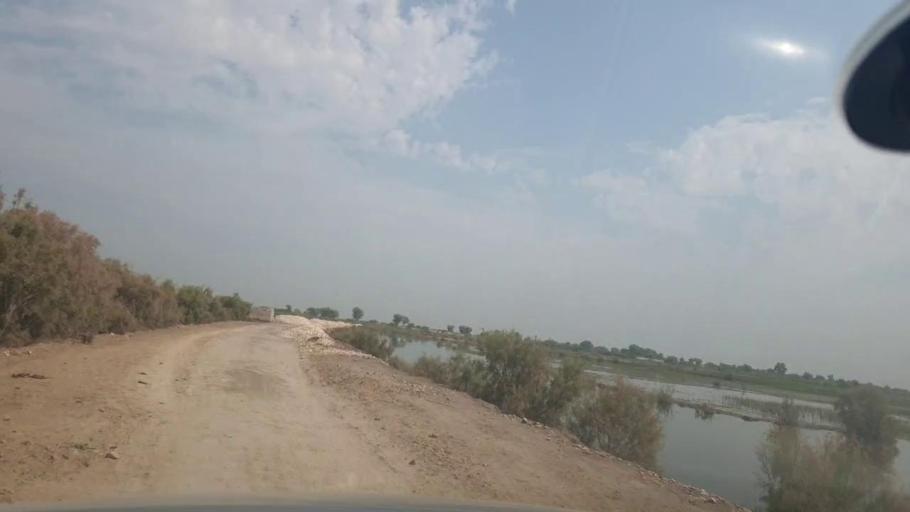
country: PK
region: Balochistan
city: Mehrabpur
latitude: 28.1123
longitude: 68.0903
